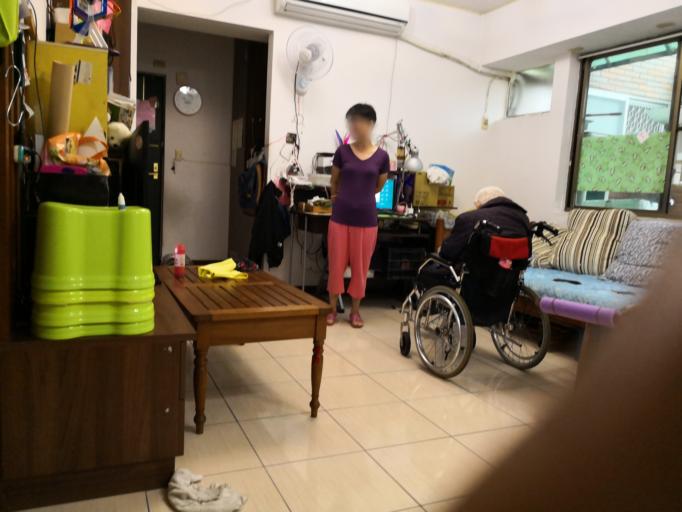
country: TW
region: Taipei
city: Taipei
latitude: 25.1275
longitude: 121.4642
